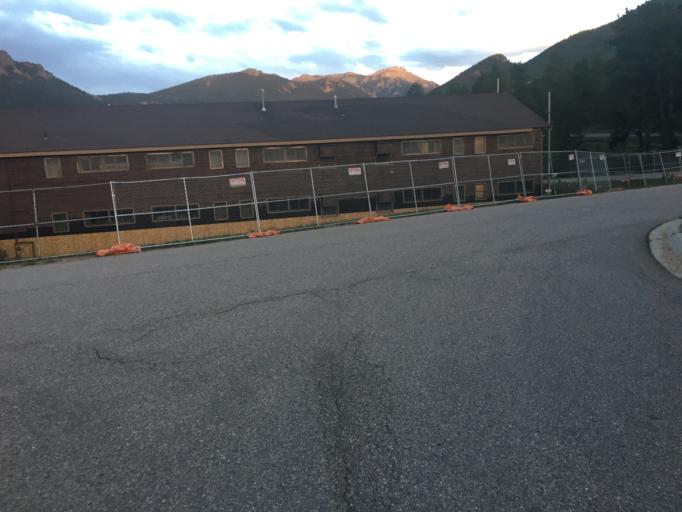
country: US
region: Colorado
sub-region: Larimer County
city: Estes Park
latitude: 40.3374
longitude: -105.5736
